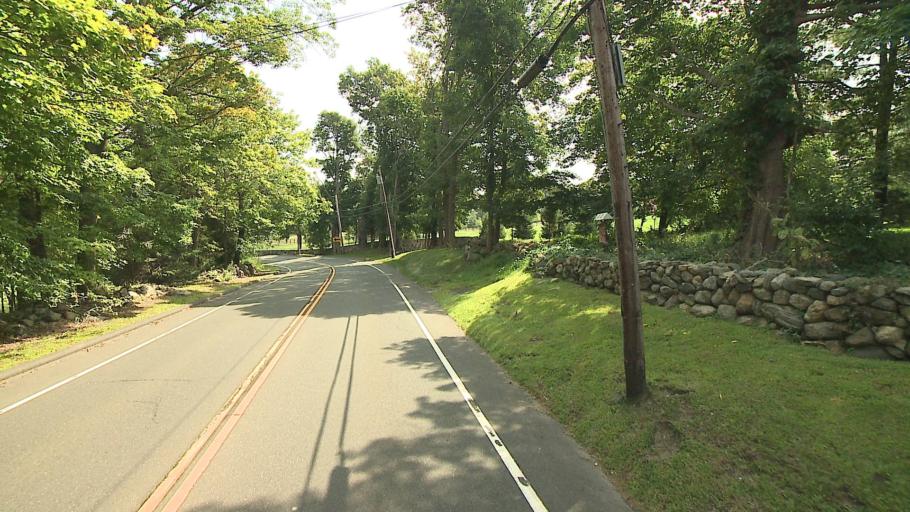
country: US
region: New York
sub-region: Putnam County
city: Peach Lake
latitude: 41.3253
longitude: -73.5381
